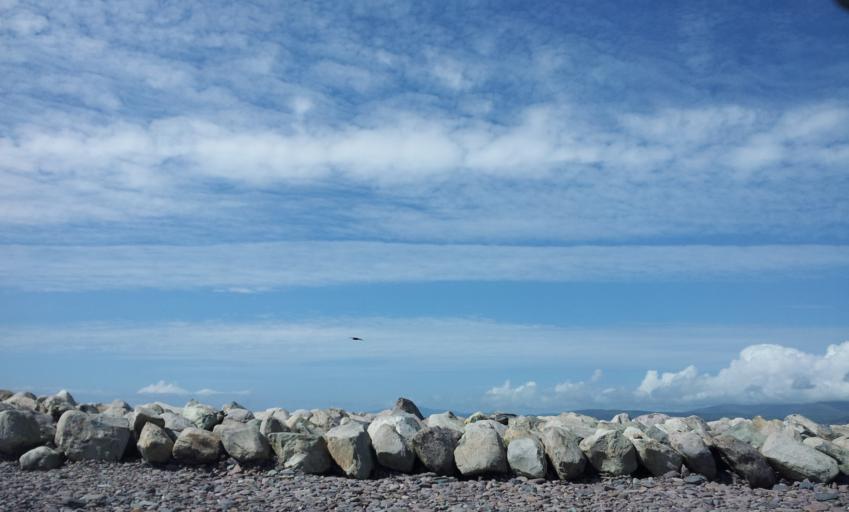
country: IE
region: Munster
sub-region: Ciarrai
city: Killorglin
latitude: 52.0580
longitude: -9.9747
